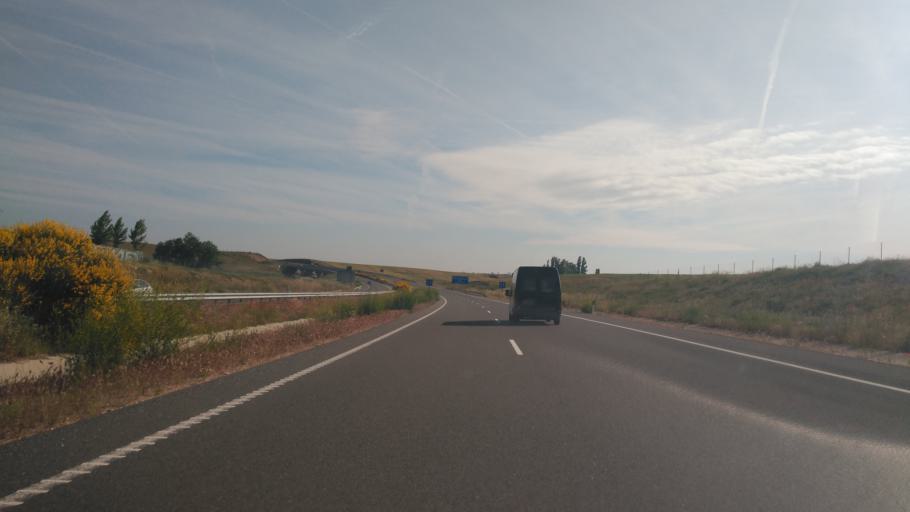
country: ES
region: Castille and Leon
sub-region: Provincia de Salamanca
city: Monterrubio de Armuna
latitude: 41.0345
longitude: -5.6701
